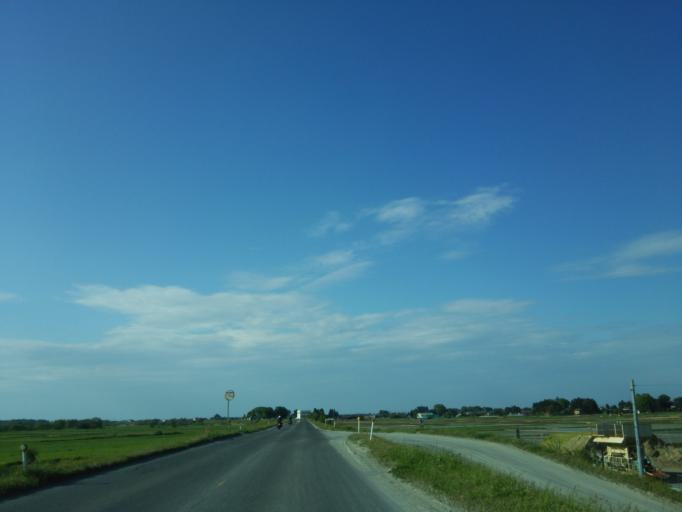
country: JP
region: Niigata
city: Niitsu-honcho
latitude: 37.7931
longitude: 139.1841
